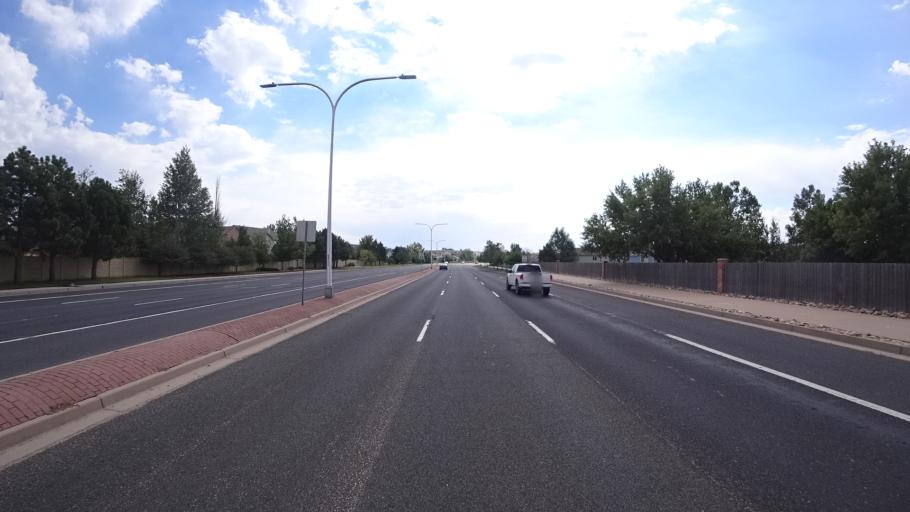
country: US
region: Colorado
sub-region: El Paso County
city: Cimarron Hills
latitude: 38.9124
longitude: -104.6941
